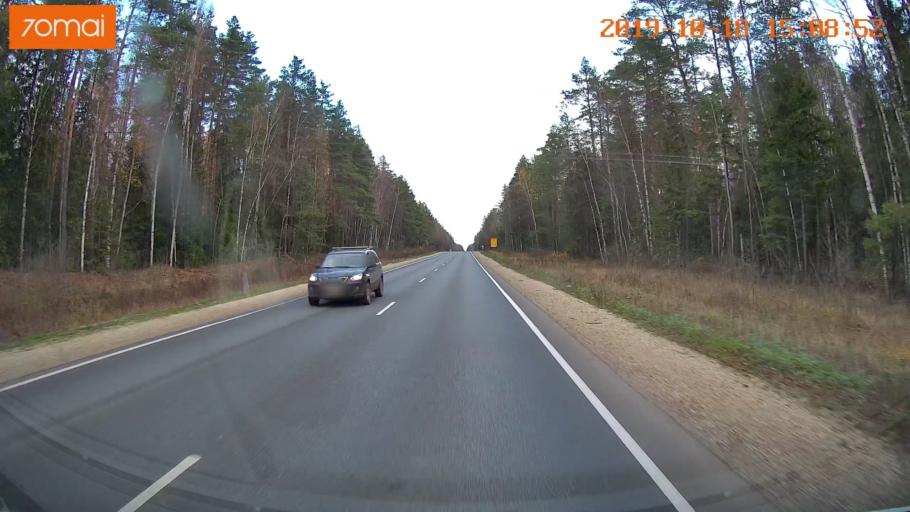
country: RU
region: Vladimir
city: Gus'-Khrustal'nyy
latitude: 55.5581
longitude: 40.6150
